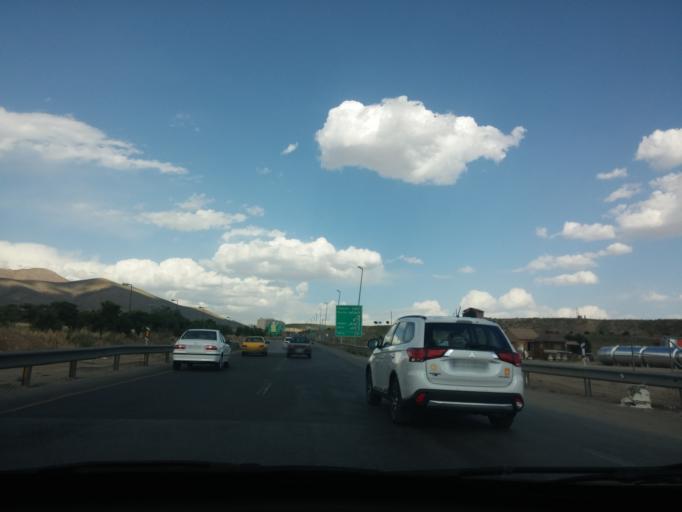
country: IR
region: Tehran
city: Damavand
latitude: 35.7188
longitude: 51.9219
